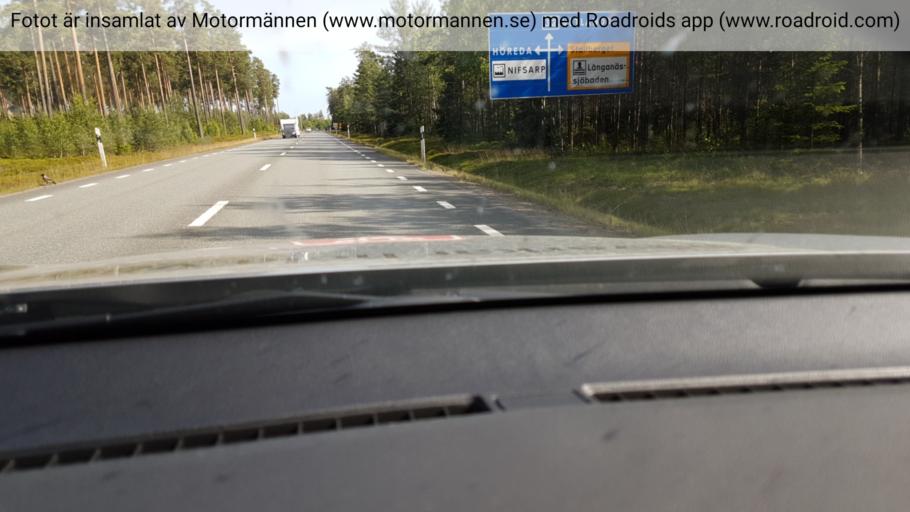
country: SE
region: Joenkoeping
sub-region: Eksjo Kommun
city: Eksjoe
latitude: 57.6400
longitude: 14.9640
